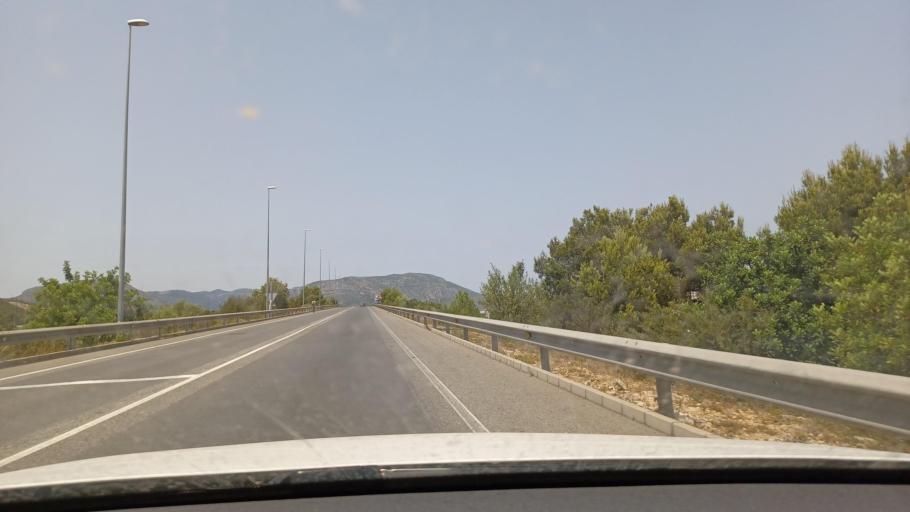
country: ES
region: Catalonia
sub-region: Provincia de Tarragona
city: Colldejou
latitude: 41.0008
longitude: 0.9169
